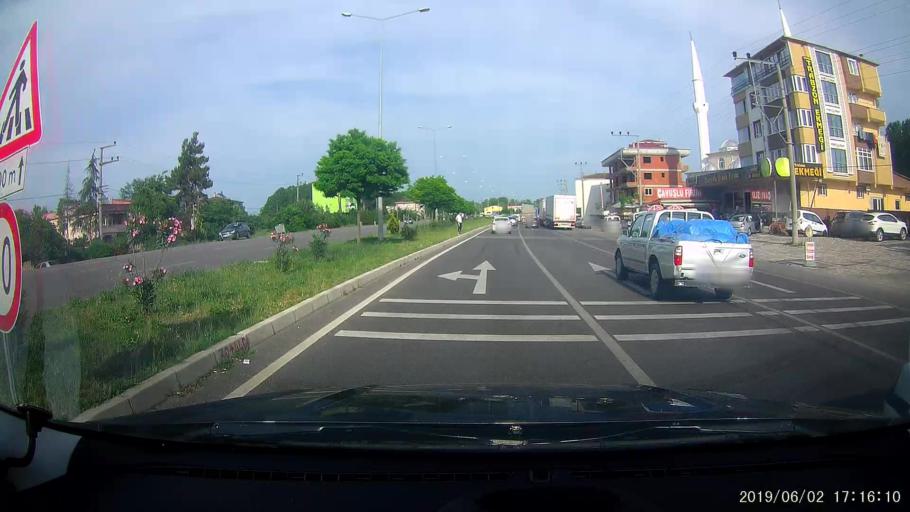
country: TR
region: Samsun
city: Dikbiyik
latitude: 41.2343
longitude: 36.5658
